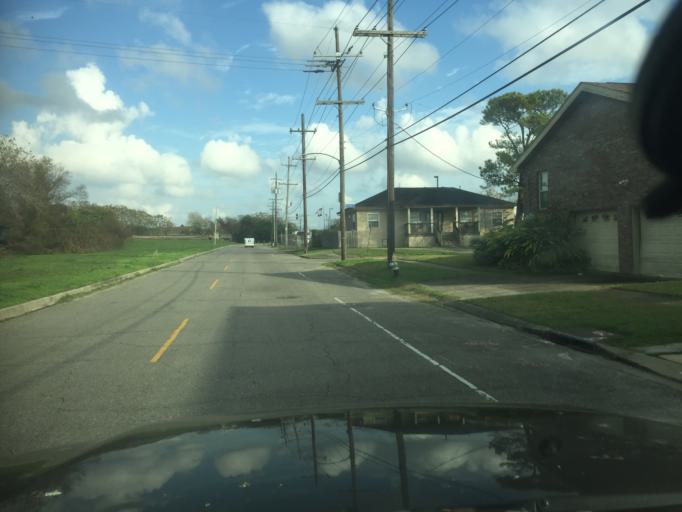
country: US
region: Louisiana
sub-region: Orleans Parish
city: New Orleans
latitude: 29.9920
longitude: -90.0793
